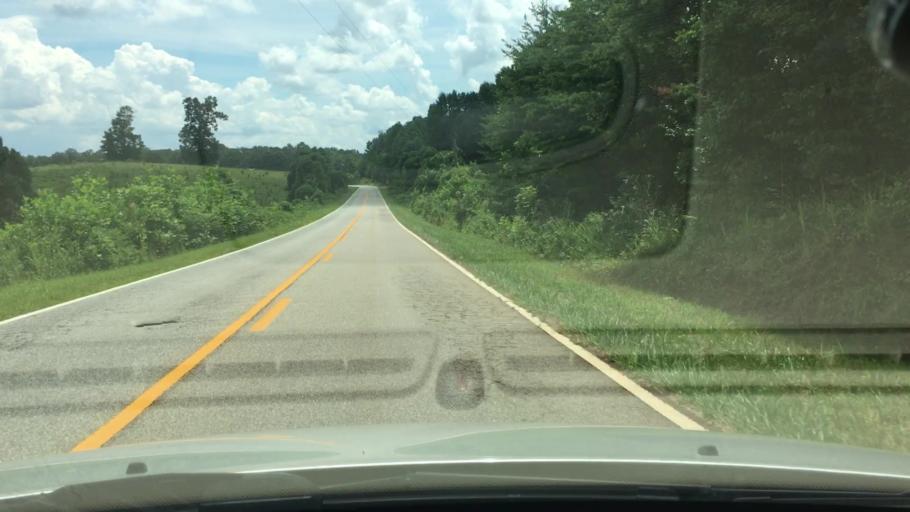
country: US
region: Georgia
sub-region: Lumpkin County
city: Dahlonega
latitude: 34.6014
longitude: -83.8960
